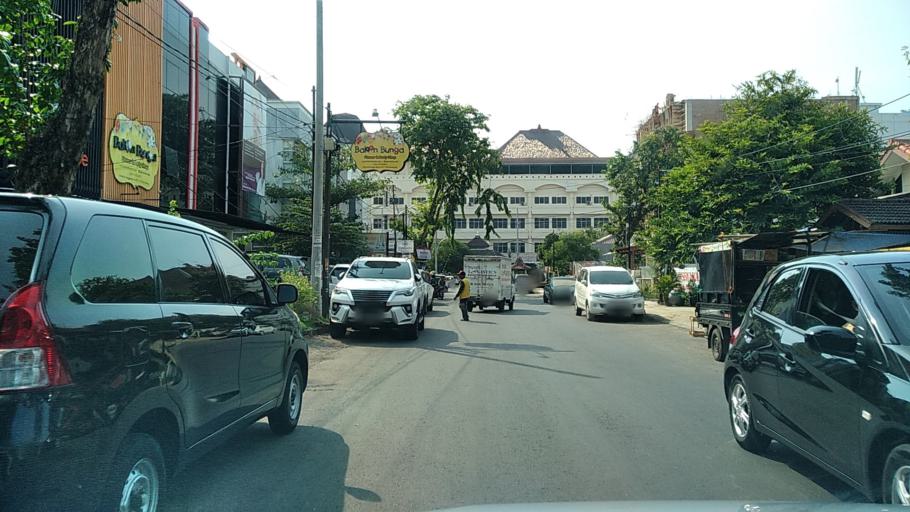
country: ID
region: Central Java
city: Semarang
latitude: -6.9933
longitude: 110.4238
